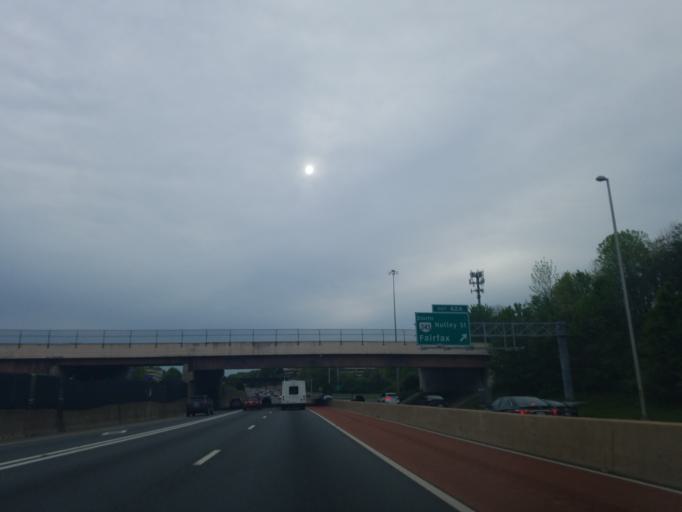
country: US
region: Virginia
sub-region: Fairfax County
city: Vienna
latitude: 38.8787
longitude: -77.2661
